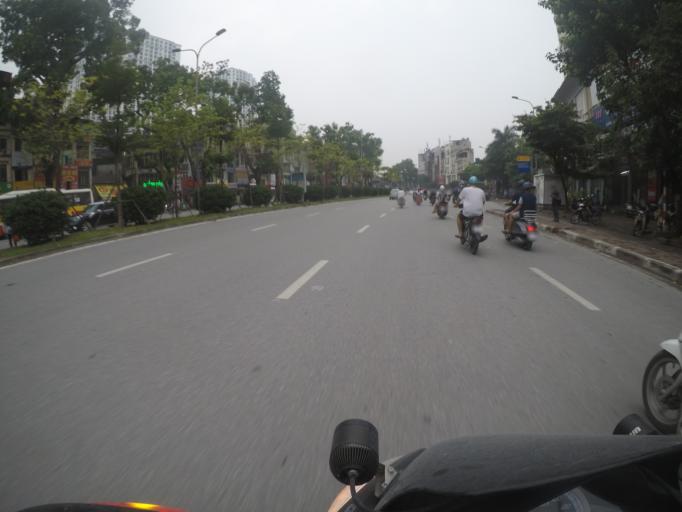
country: VN
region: Ha Noi
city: Dong Da
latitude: 21.0038
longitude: 105.8187
